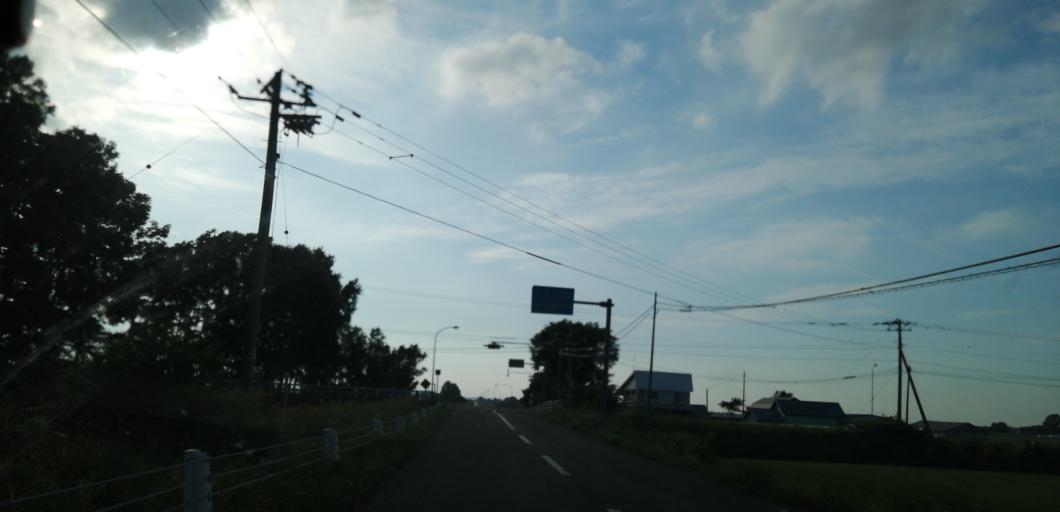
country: JP
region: Hokkaido
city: Kitahiroshima
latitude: 42.9440
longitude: 141.6874
